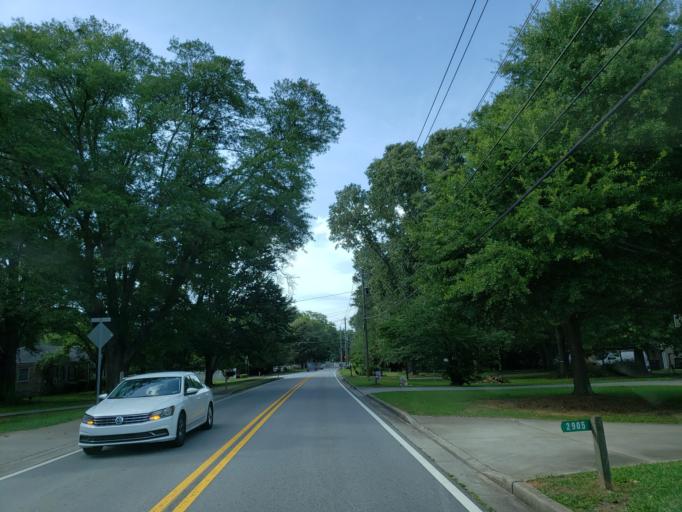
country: US
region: Georgia
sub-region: Cobb County
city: Powder Springs
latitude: 33.8830
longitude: -84.6845
